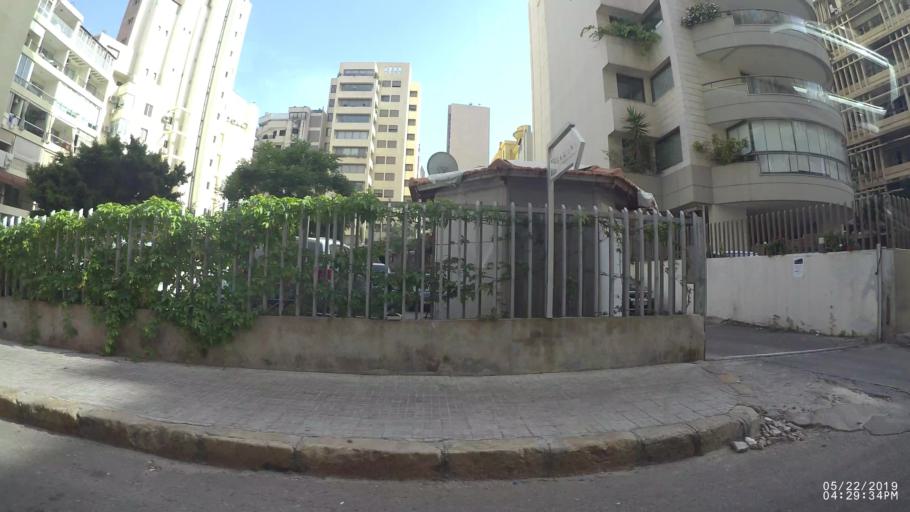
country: LB
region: Beyrouth
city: Beirut
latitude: 33.8976
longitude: 35.4932
